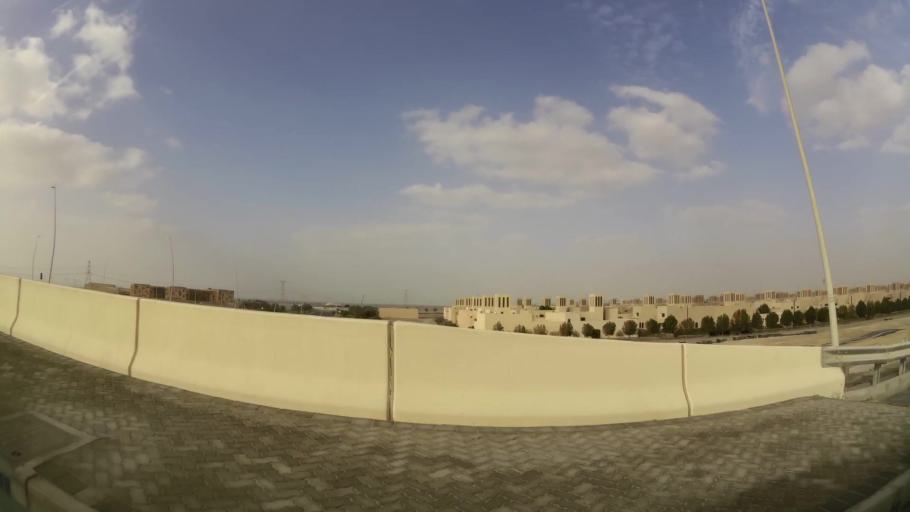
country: AE
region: Abu Dhabi
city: Abu Dhabi
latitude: 24.5000
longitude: 54.5927
